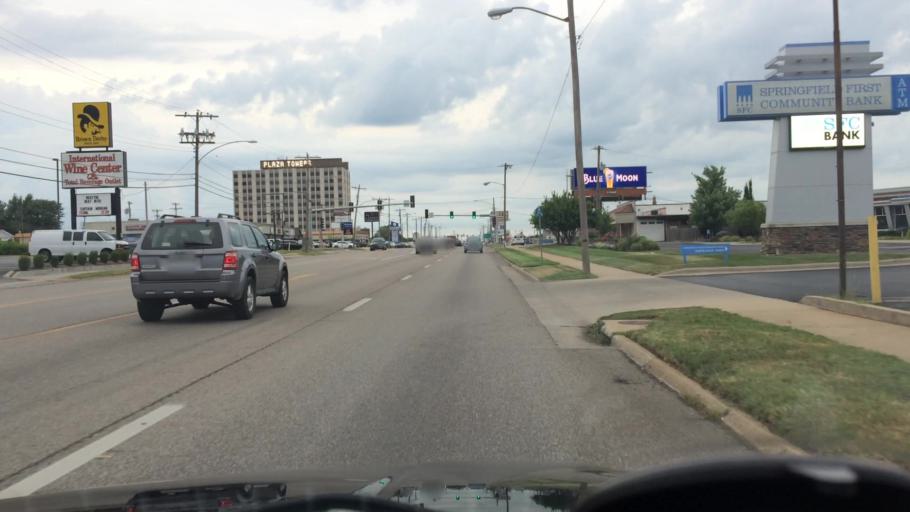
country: US
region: Missouri
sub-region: Greene County
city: Springfield
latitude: 37.1771
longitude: -93.2624
